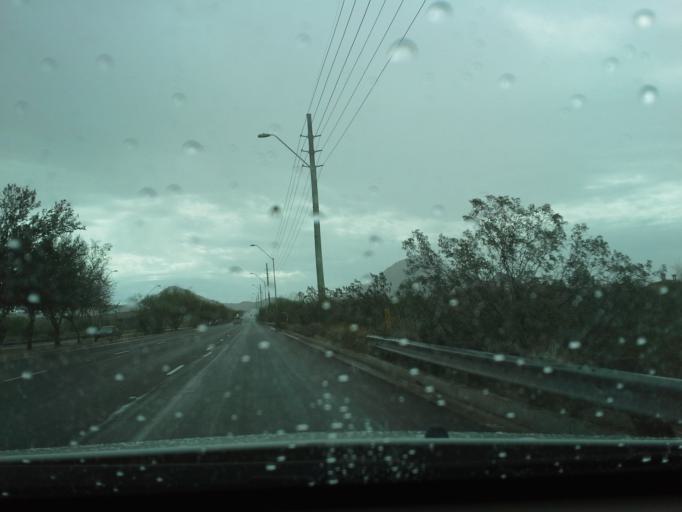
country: US
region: Arizona
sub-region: Maricopa County
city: Fountain Hills
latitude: 33.5823
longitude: -111.8109
